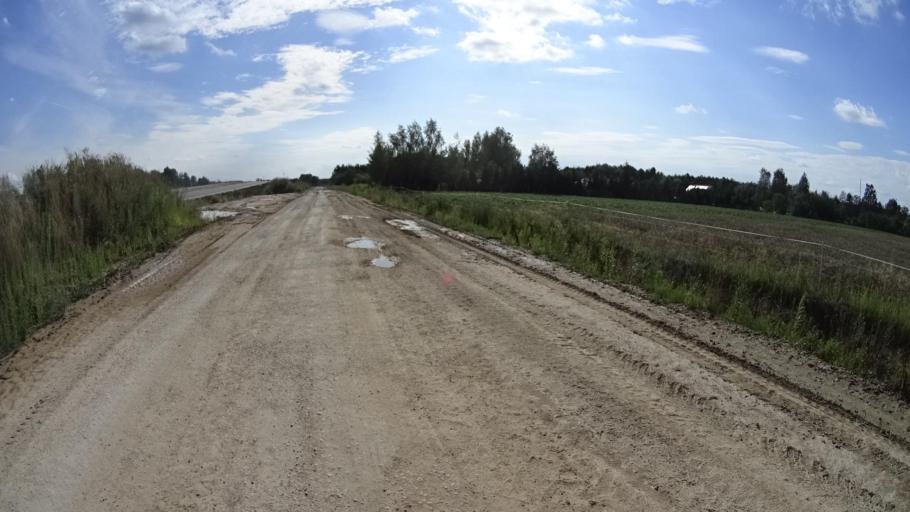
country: PL
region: Masovian Voivodeship
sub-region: Powiat piaseczynski
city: Lesznowola
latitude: 52.0582
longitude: 20.9288
